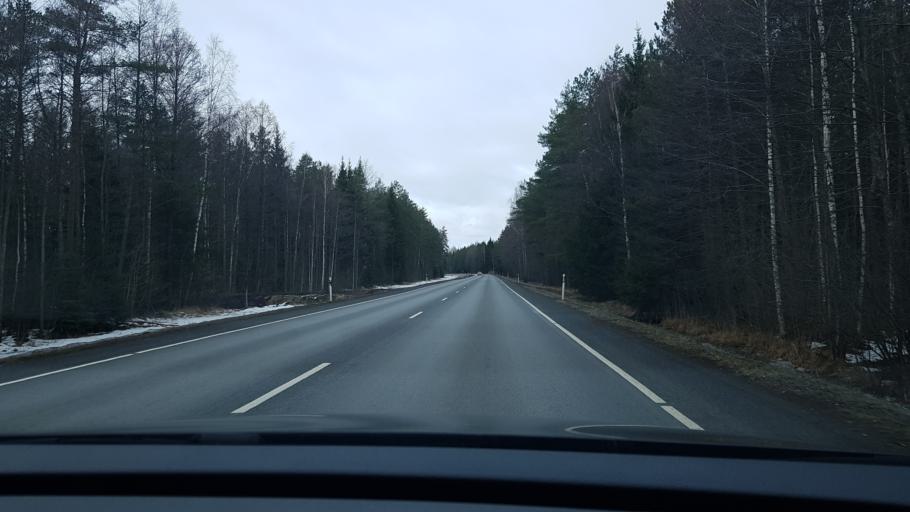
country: EE
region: Paernumaa
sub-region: Paikuse vald
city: Paikuse
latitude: 58.2478
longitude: 24.6871
